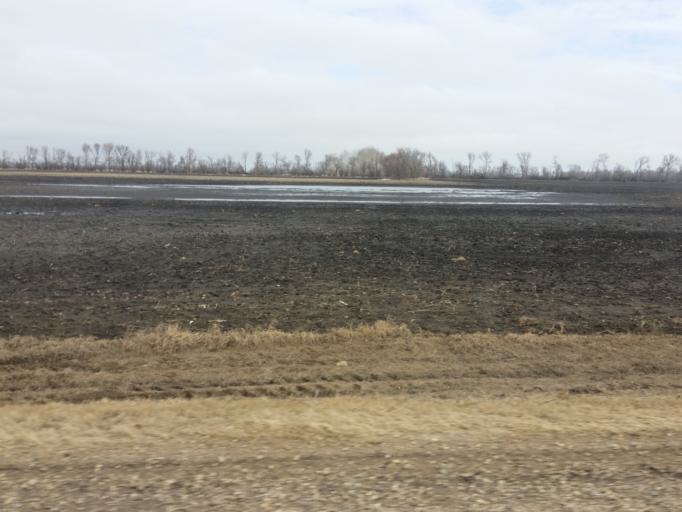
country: US
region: North Dakota
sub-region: Walsh County
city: Grafton
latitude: 48.4202
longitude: -97.3212
